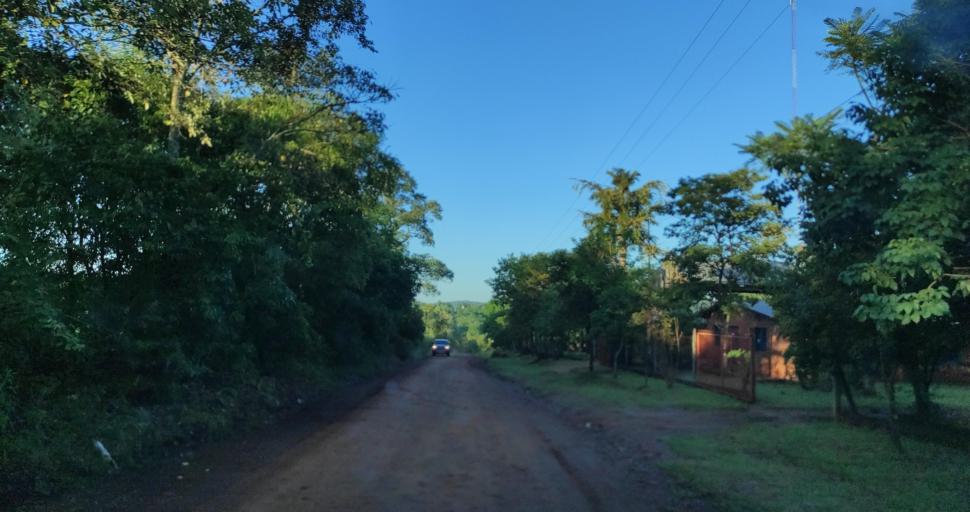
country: AR
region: Misiones
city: Gobernador Roca
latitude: -27.2241
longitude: -55.4310
